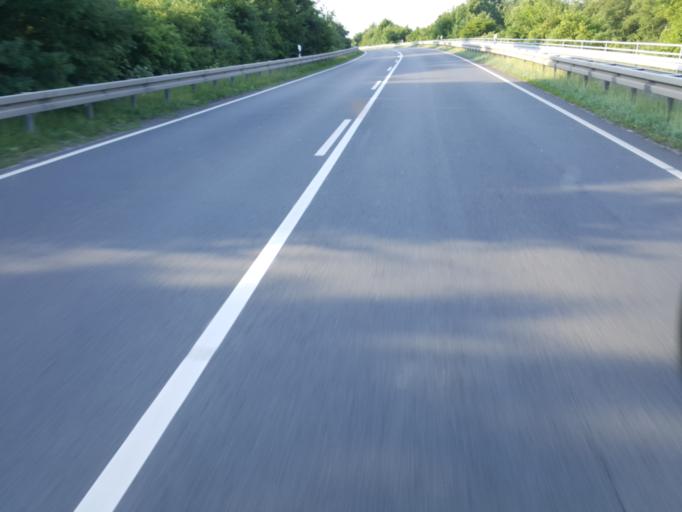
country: DE
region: Lower Saxony
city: Leese
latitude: 52.5232
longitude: 9.1228
